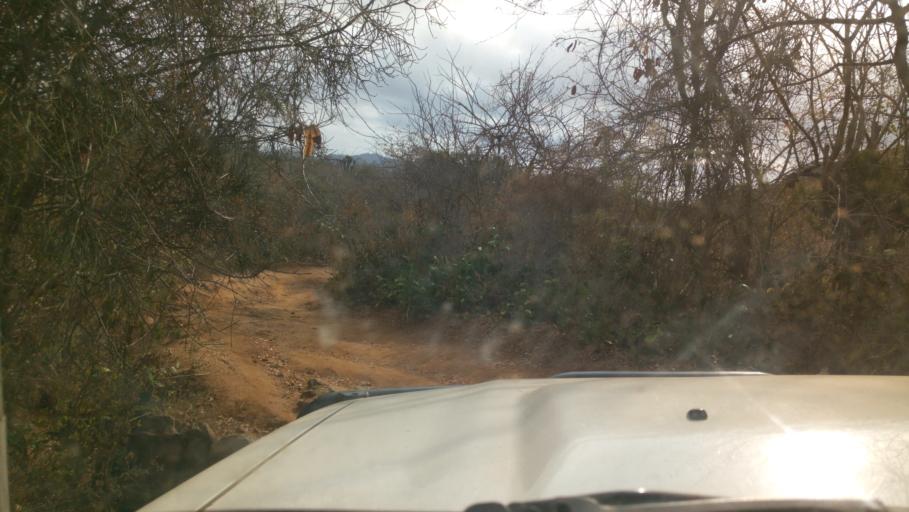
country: KE
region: Kitui
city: Kitui
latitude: -1.8556
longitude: 38.2496
